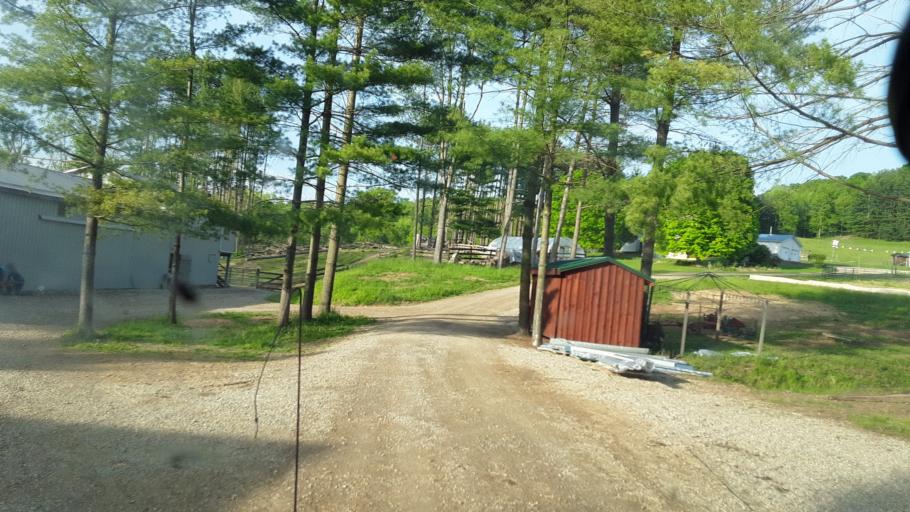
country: US
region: Ohio
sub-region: Fairfield County
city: Lancaster
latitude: 39.5185
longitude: -82.6924
